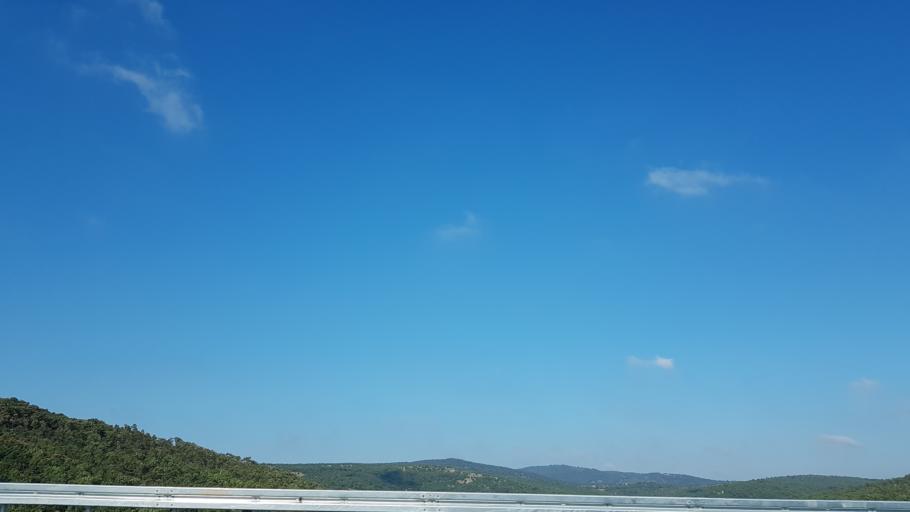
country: TR
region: Balikesir
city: Ertugrul
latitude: 39.5325
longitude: 27.6760
